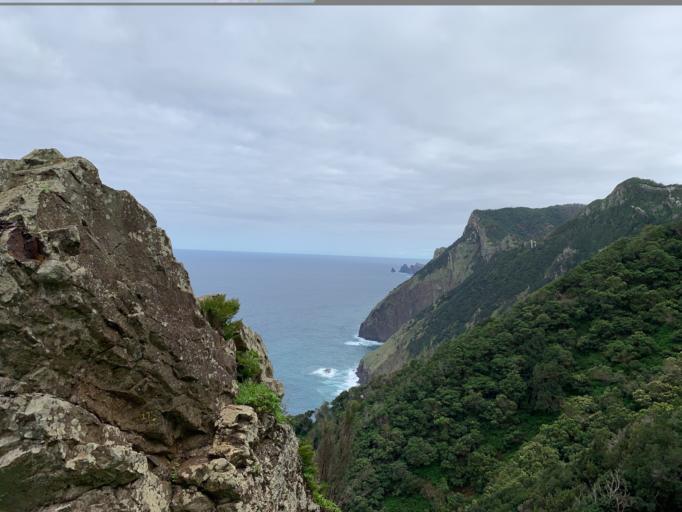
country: PT
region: Madeira
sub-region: Machico
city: Canical
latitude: 32.7592
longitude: -16.7878
